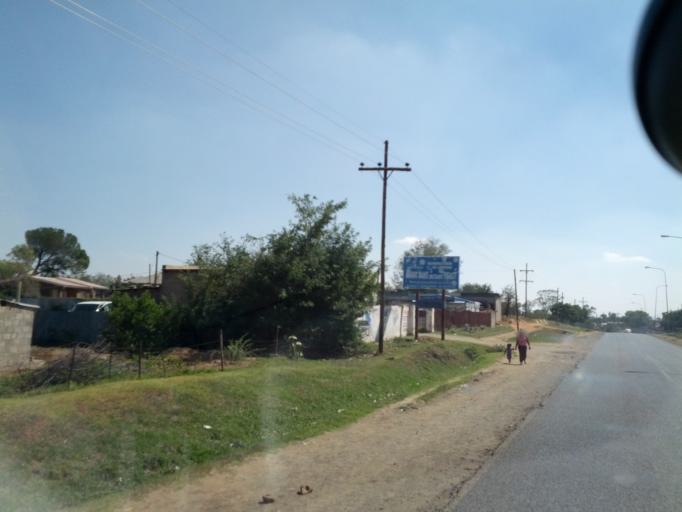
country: LS
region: Berea
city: Teyateyaneng
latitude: -29.1438
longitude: 27.7498
